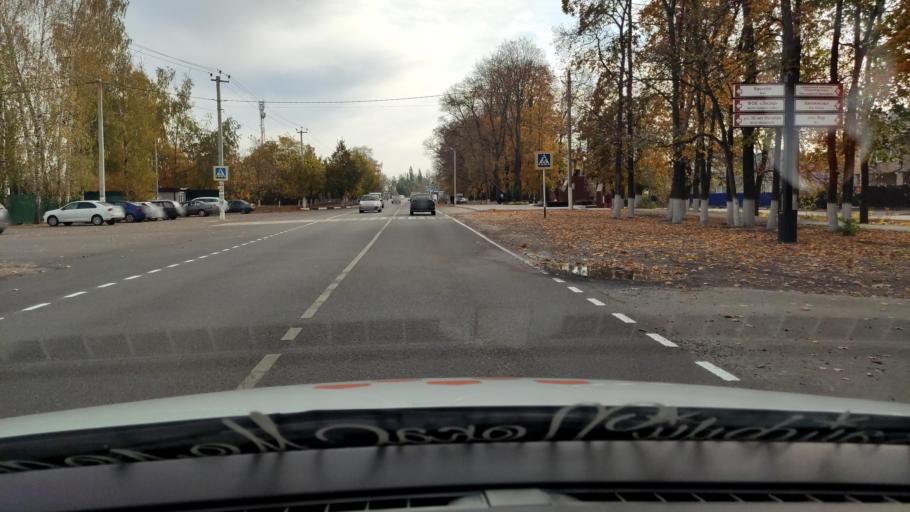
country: RU
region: Voronezj
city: Ramon'
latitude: 51.9110
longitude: 39.3279
